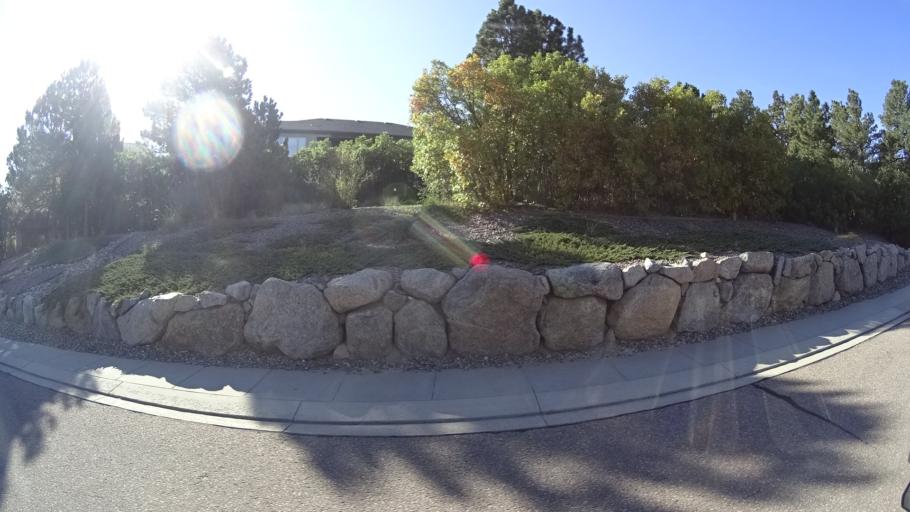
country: US
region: Colorado
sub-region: El Paso County
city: Colorado Springs
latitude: 38.9030
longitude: -104.7933
